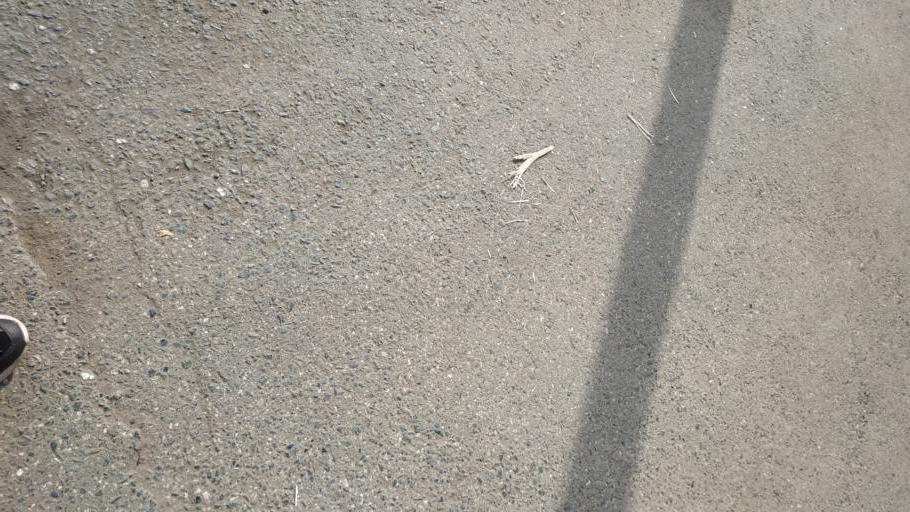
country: RU
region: Tomsk
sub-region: Tomskiy Rayon
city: Tomsk
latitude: 56.4712
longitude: 84.9845
